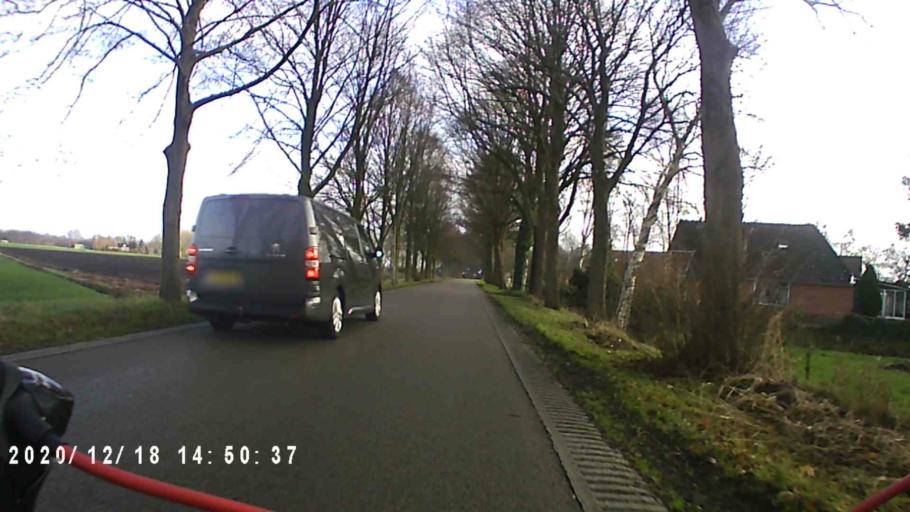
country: NL
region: Groningen
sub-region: Gemeente Haren
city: Haren
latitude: 53.1962
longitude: 6.6715
